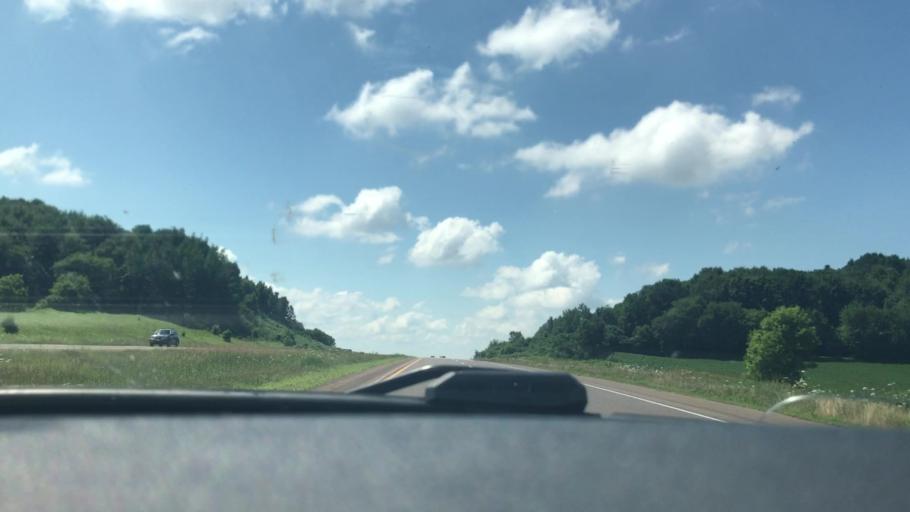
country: US
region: Wisconsin
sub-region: Chippewa County
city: Chippewa Falls
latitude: 44.9579
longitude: -91.4256
